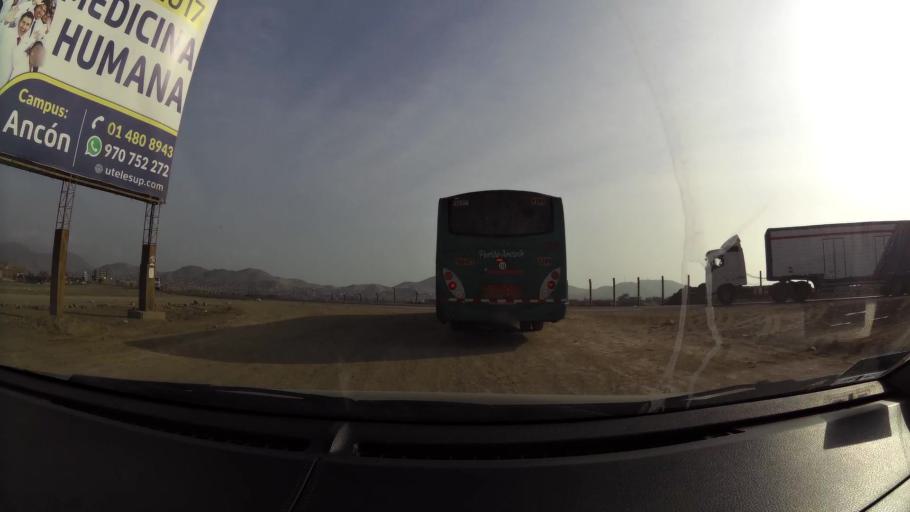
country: PE
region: Lima
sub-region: Lima
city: Santa Rosa
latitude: -11.7627
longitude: -77.1615
